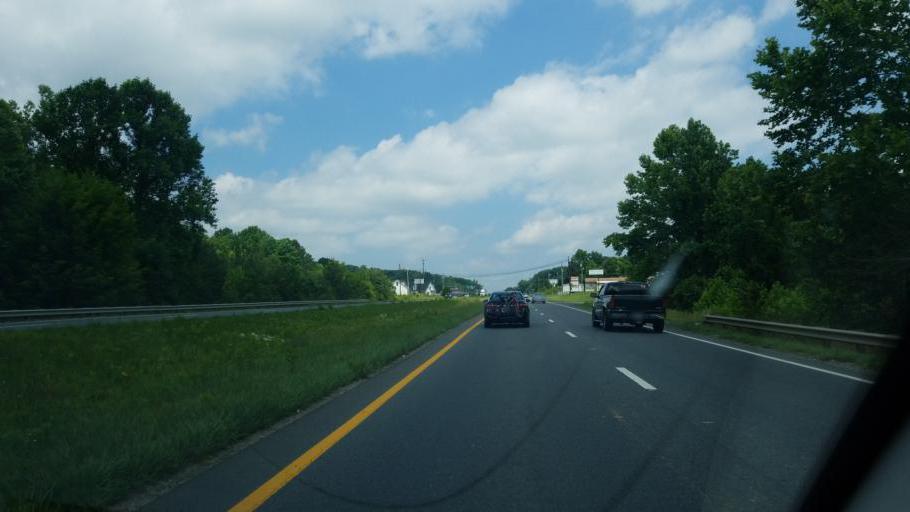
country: US
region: Virginia
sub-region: Campbell County
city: Rustburg
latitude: 37.2905
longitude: -79.1688
